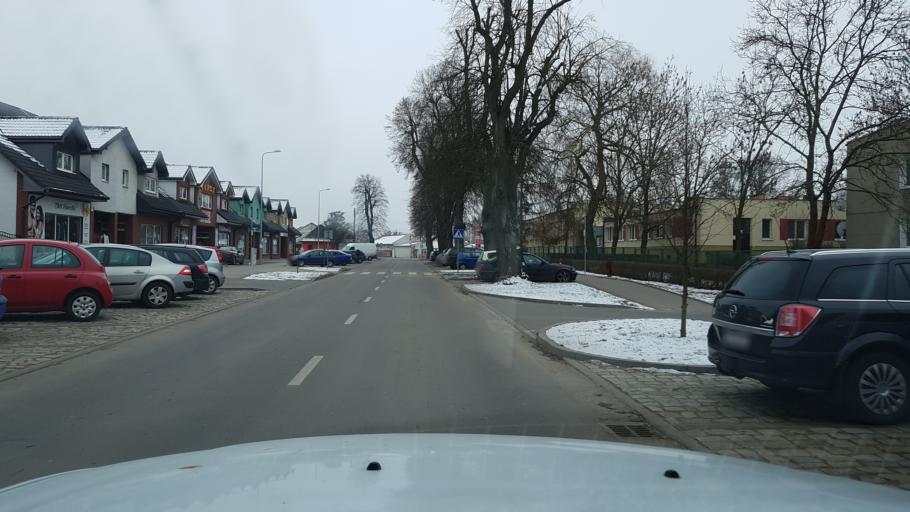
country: PL
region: West Pomeranian Voivodeship
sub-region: Powiat gryfinski
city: Chojna
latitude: 52.9627
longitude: 14.4438
